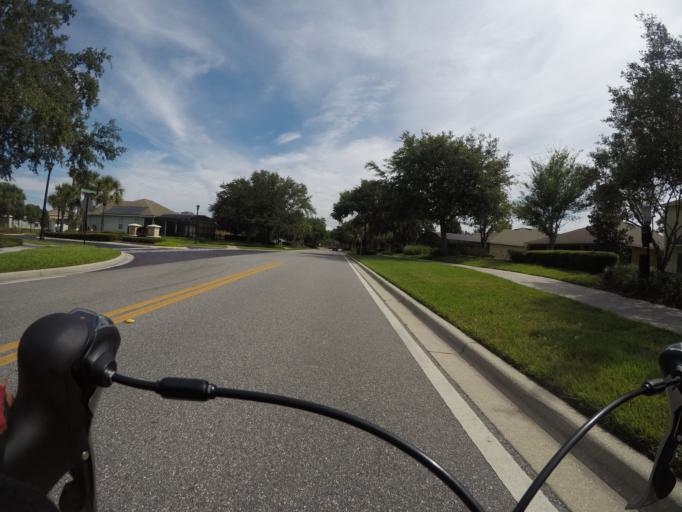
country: US
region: Florida
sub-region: Orange County
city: Conway
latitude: 28.4074
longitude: -81.2205
